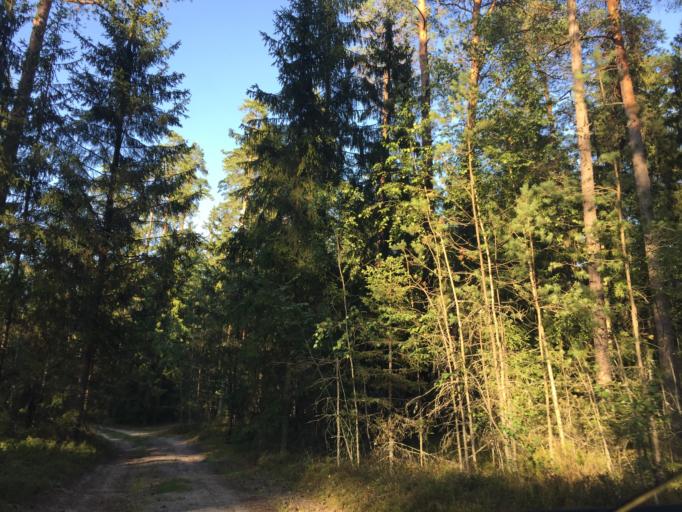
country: LV
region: Garkalne
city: Garkalne
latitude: 57.0069
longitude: 24.4356
